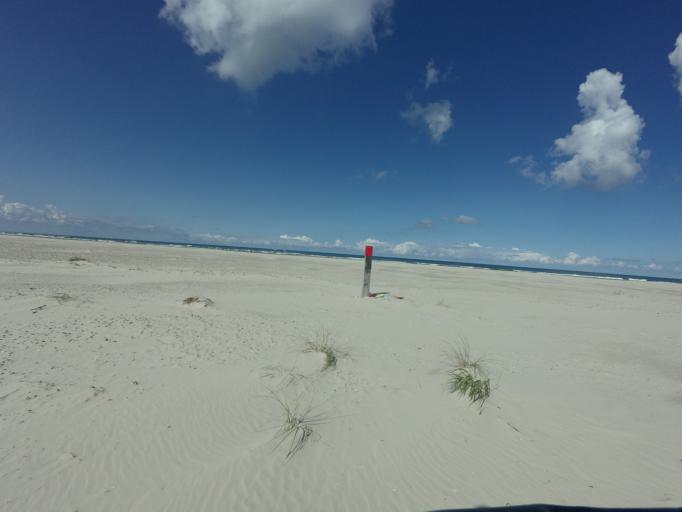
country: NL
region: Friesland
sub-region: Gemeente Terschelling
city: West-Terschelling
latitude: 53.3924
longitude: 5.1997
